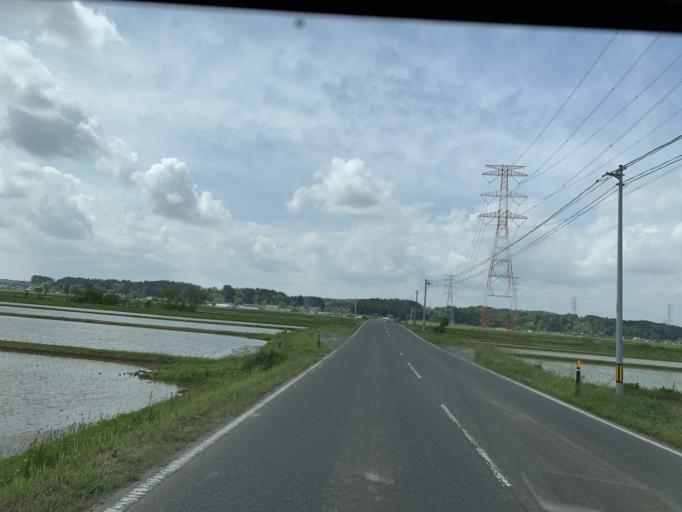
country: JP
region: Iwate
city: Ichinoseki
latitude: 38.7990
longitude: 141.0077
